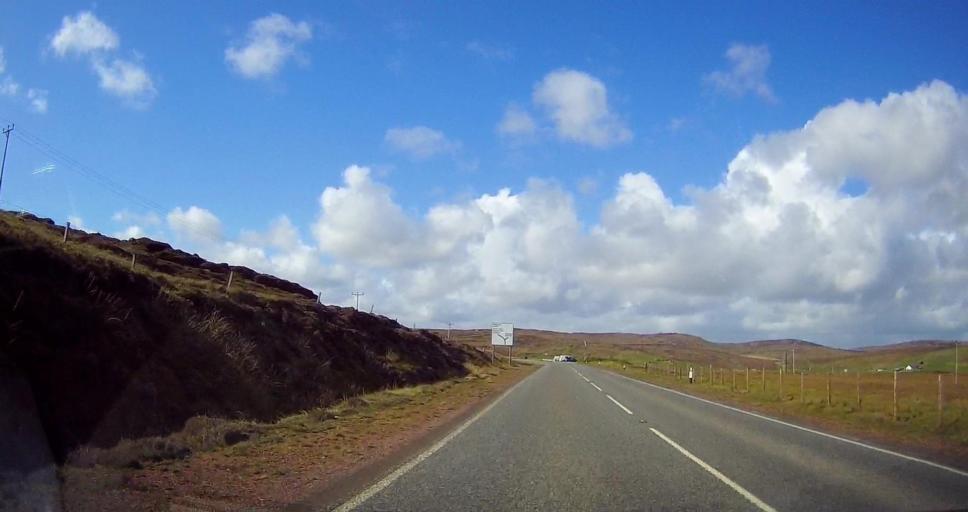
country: GB
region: Scotland
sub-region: Shetland Islands
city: Lerwick
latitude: 60.2623
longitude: -1.2221
